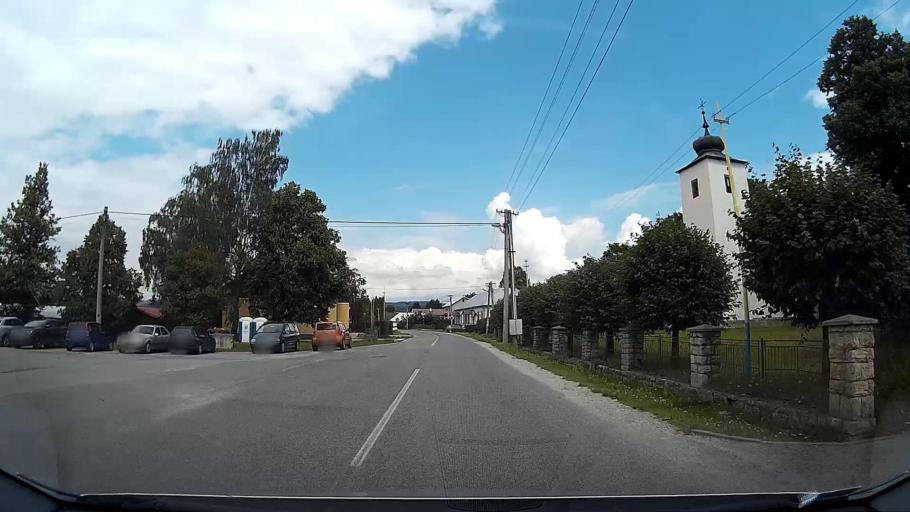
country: SK
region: Presovsky
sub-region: Okres Poprad
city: Poprad
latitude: 48.9798
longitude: 20.3906
